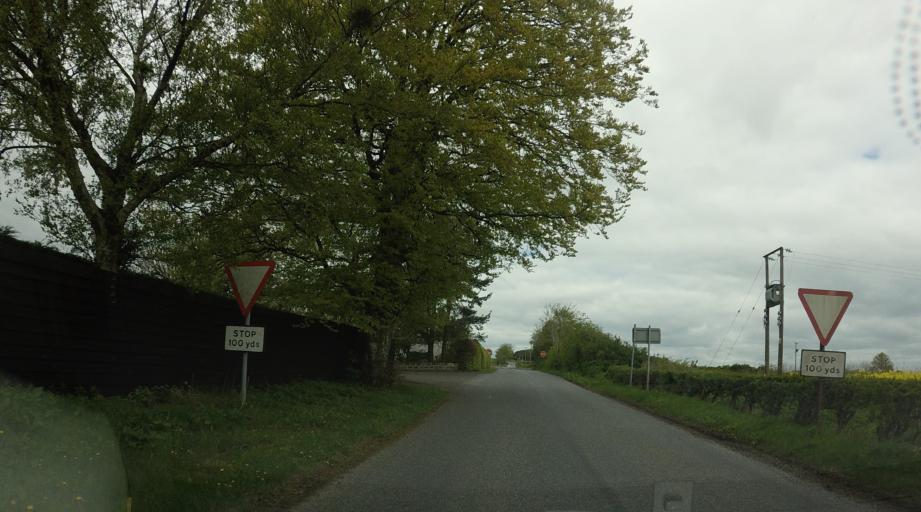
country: GB
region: Scotland
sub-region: Perth and Kinross
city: Milnathort
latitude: 56.2439
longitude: -3.3743
